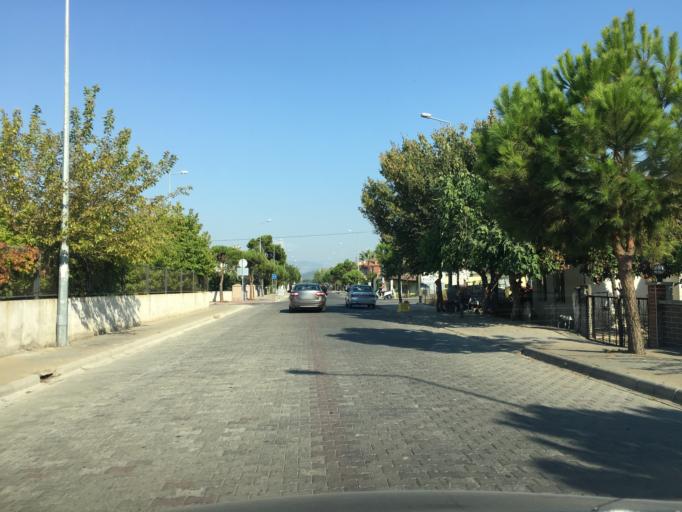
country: TR
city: Dalyan
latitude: 36.8362
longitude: 28.6493
